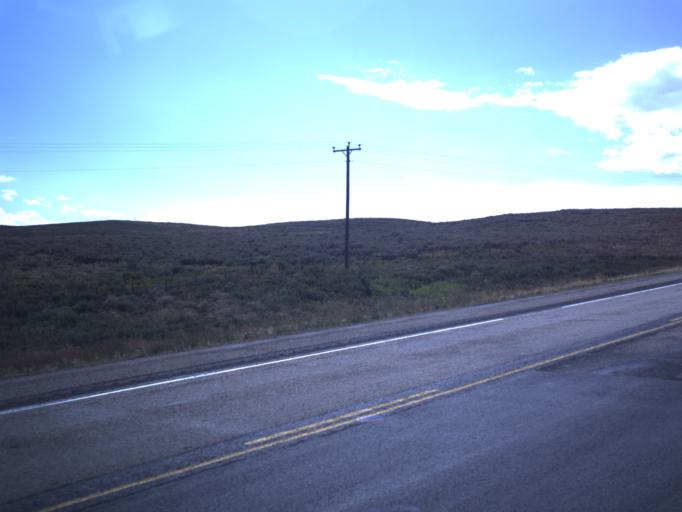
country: US
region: Utah
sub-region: Wasatch County
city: Heber
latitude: 40.1896
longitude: -111.0738
